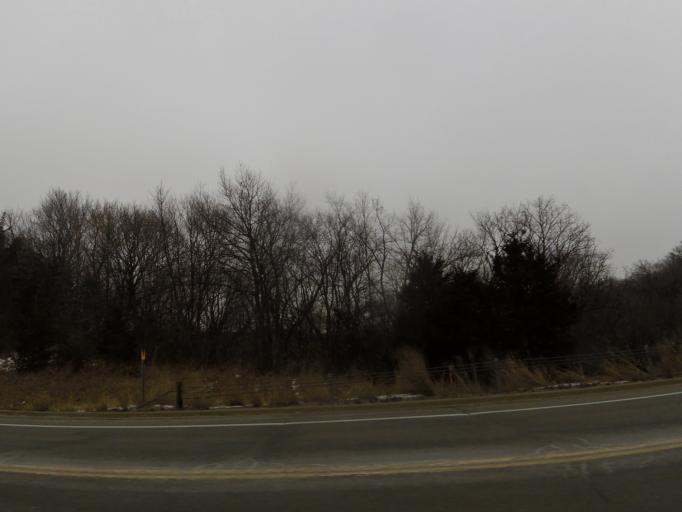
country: US
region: Minnesota
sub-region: Scott County
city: Jordan
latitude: 44.6524
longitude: -93.6285
